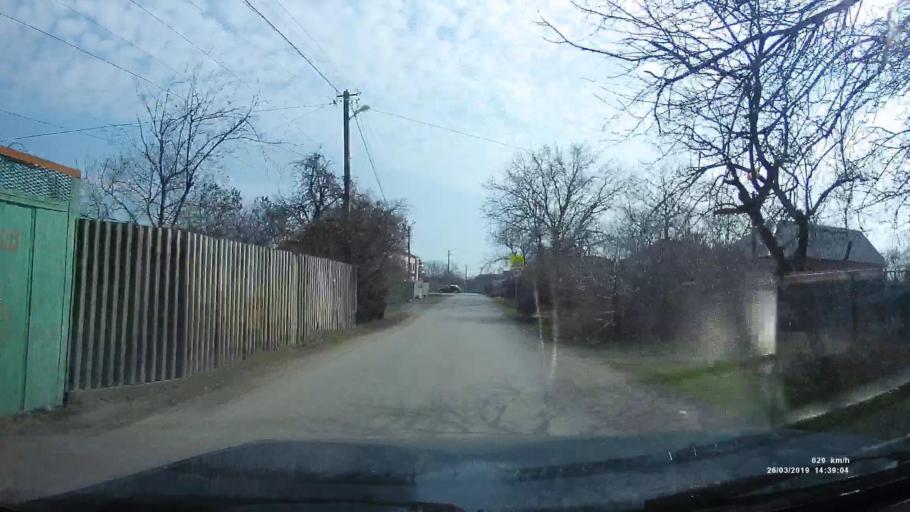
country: RU
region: Rostov
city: Novobessergenovka
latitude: 47.1798
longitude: 38.8626
